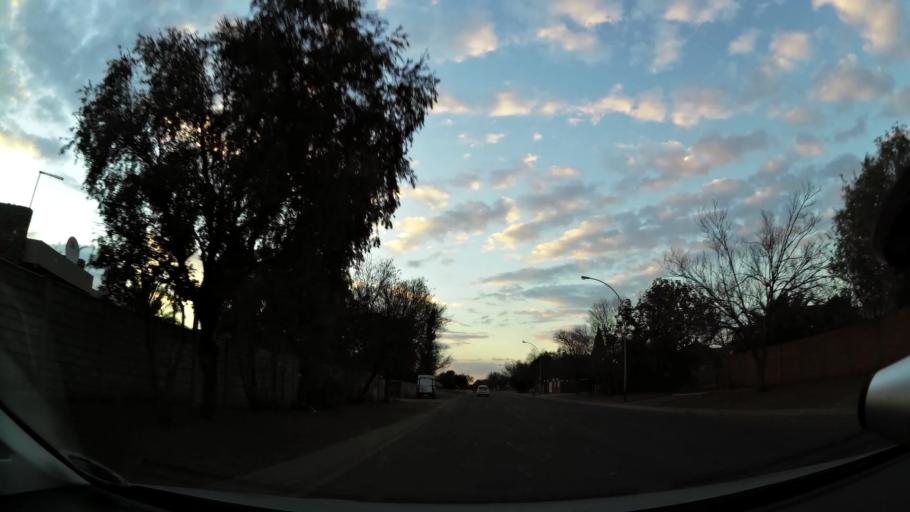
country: ZA
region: Orange Free State
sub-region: Mangaung Metropolitan Municipality
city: Bloemfontein
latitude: -29.1619
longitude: 26.1892
